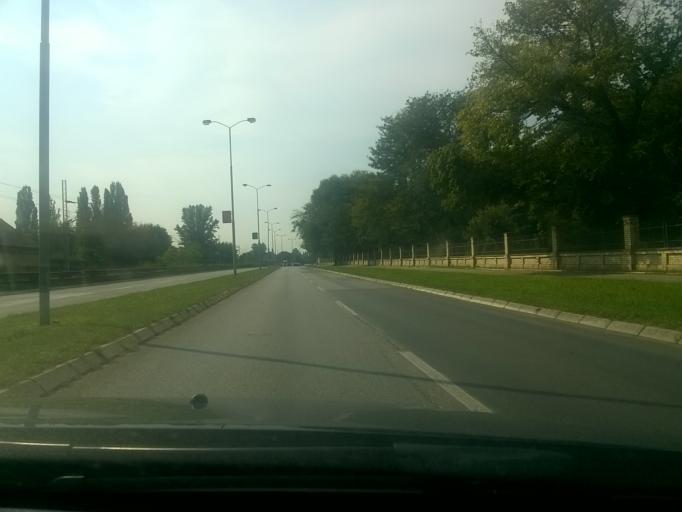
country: RS
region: Autonomna Pokrajina Vojvodina
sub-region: Juznobanatski Okrug
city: Pancevo
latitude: 44.8638
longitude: 20.6583
